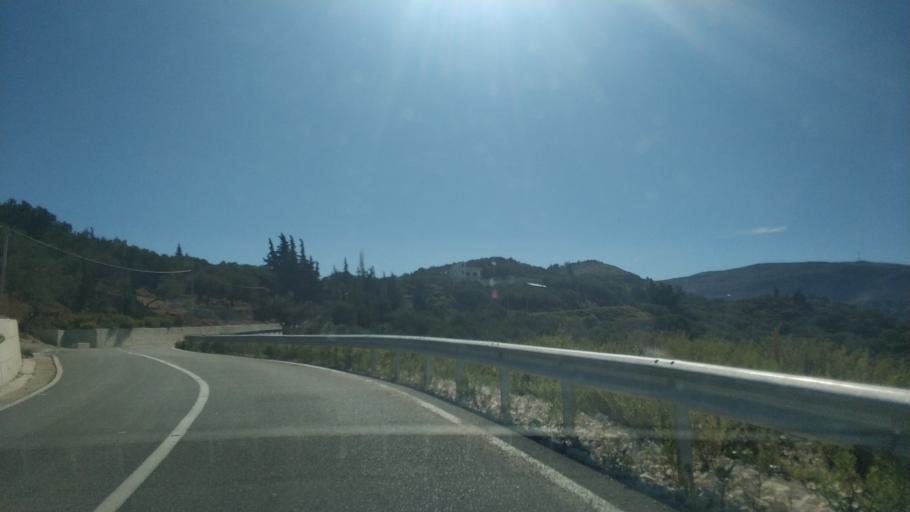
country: AL
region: Vlore
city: Vlore
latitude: 40.4559
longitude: 19.5141
